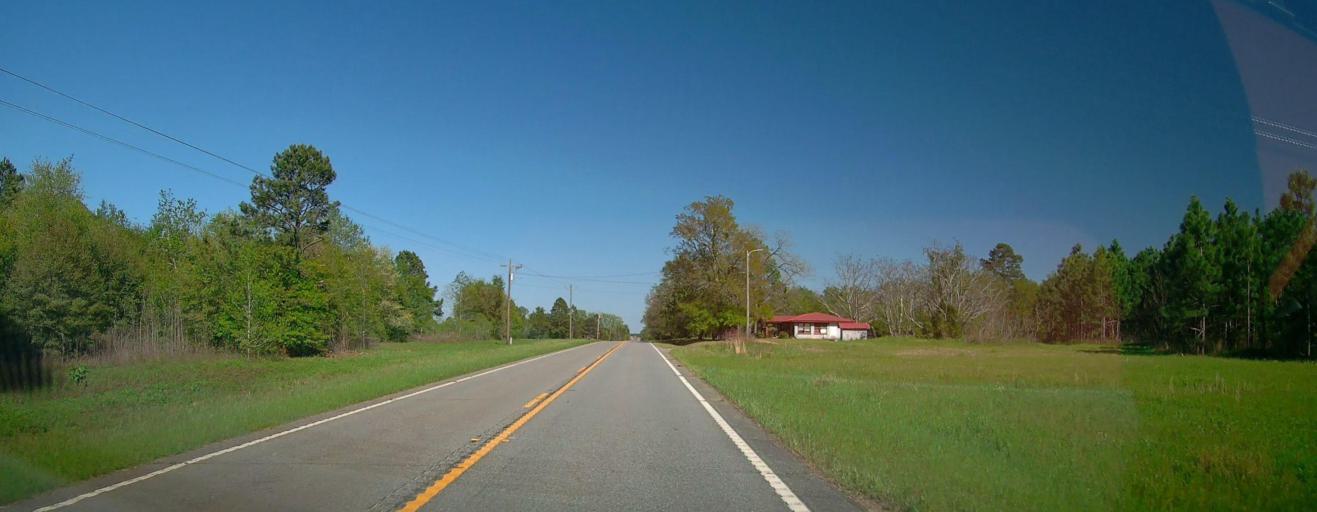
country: US
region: Georgia
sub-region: Dooly County
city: Unadilla
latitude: 32.2601
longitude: -83.6924
